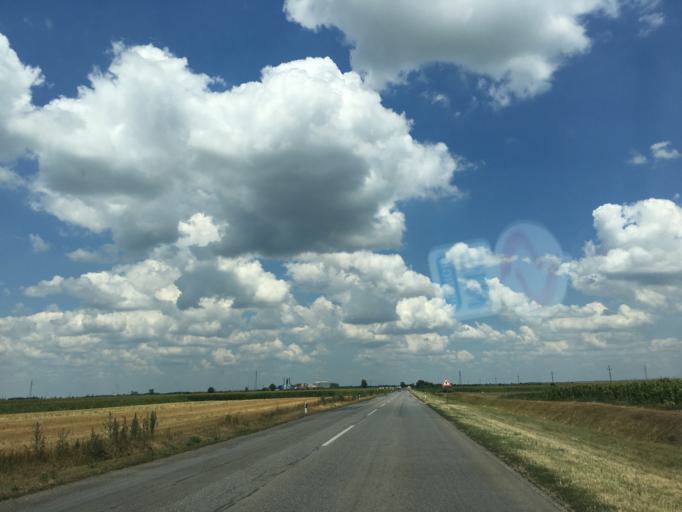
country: RS
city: Debeljaca
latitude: 45.0608
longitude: 20.6400
